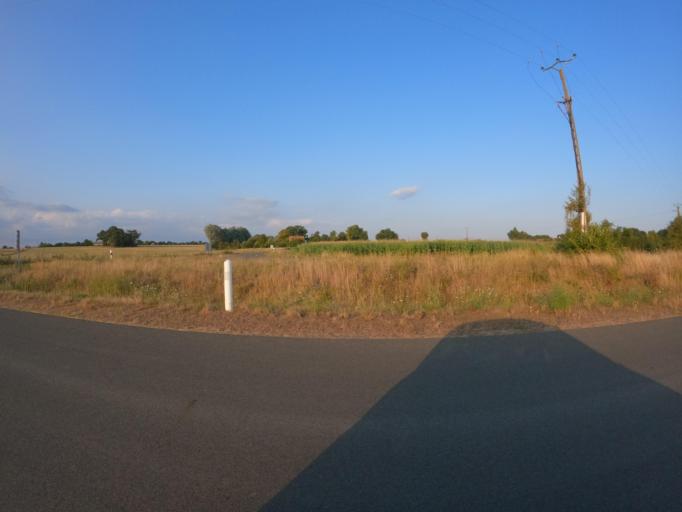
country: FR
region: Pays de la Loire
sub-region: Departement de la Sarthe
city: Brulon
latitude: 47.9150
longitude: -0.2282
